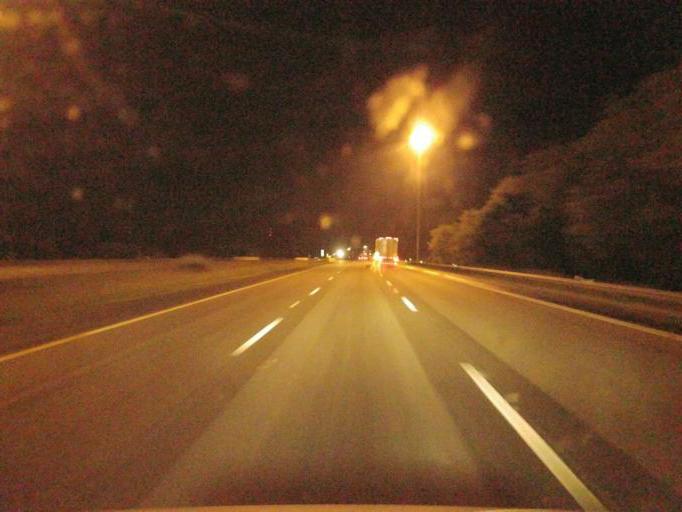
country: US
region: Ohio
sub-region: Sandusky County
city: Bellville
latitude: 40.6457
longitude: -82.5476
